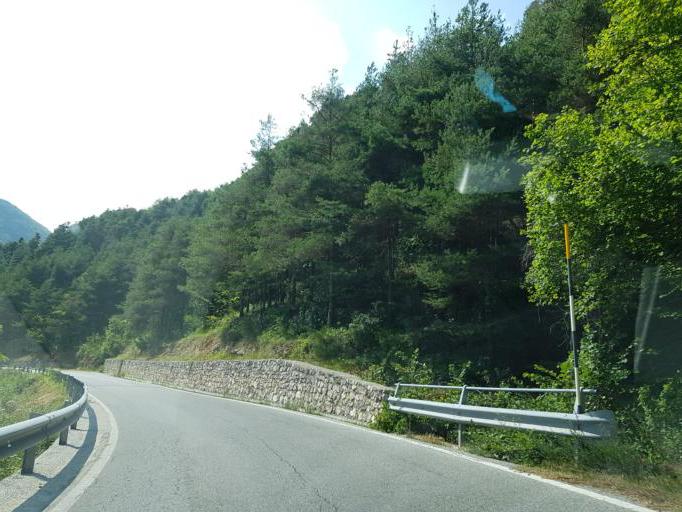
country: IT
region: Piedmont
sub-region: Provincia di Cuneo
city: Macra
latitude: 44.4944
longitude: 7.2087
